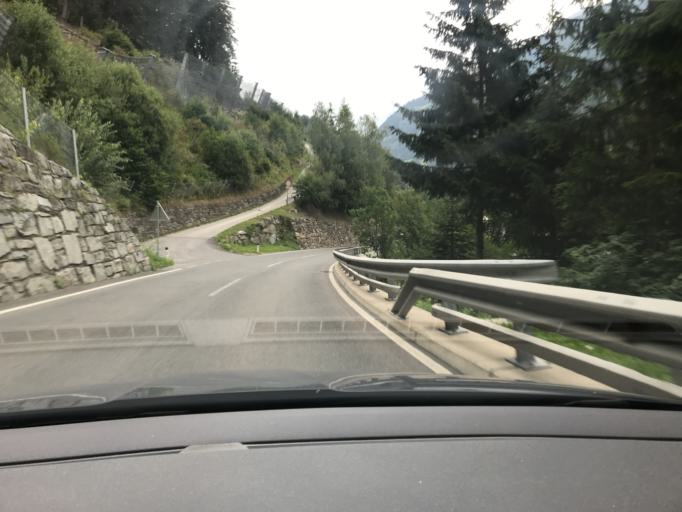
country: AT
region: Tyrol
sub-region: Politischer Bezirk Lienz
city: Hopfgarten in Defereggen
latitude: 46.9308
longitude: 12.5737
